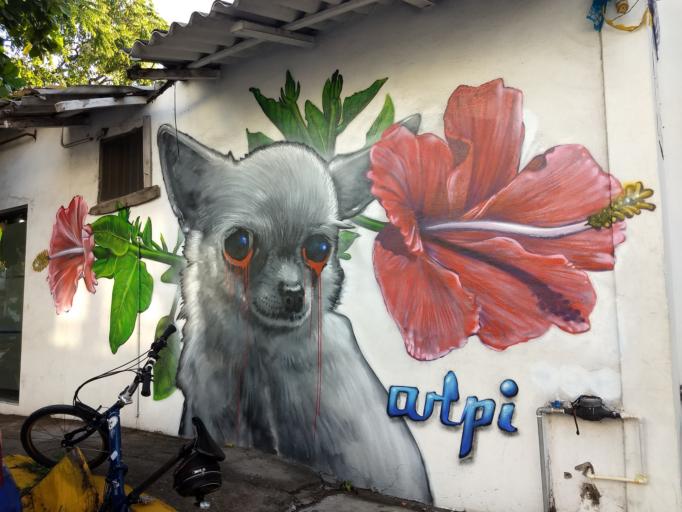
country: MX
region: Jalisco
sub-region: Puerto Vallarta
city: Puerto Vallarta
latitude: 20.6161
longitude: -105.2311
